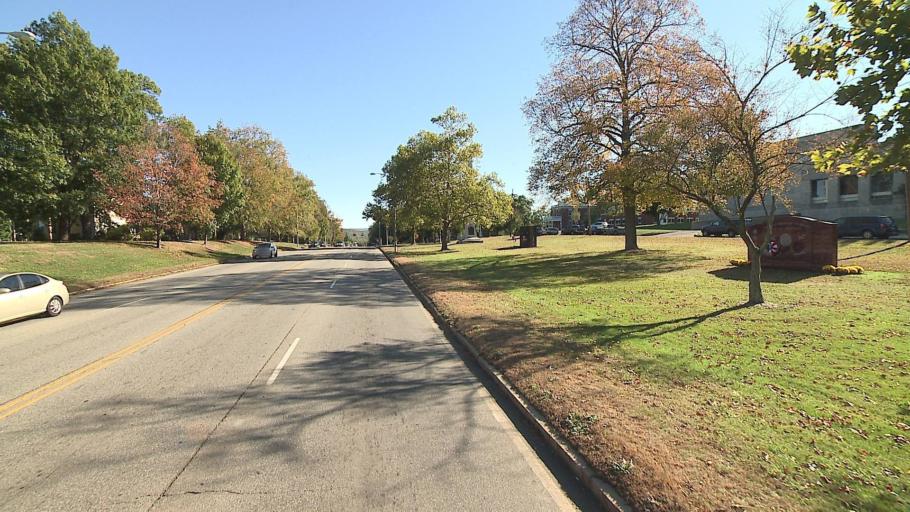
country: US
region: Connecticut
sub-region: Middlesex County
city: Middletown
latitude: 41.5599
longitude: -72.6579
